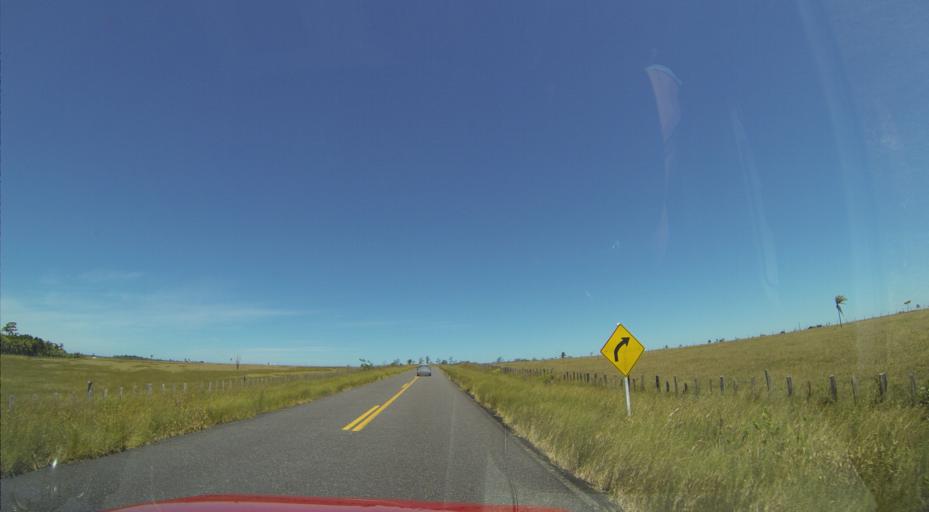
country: BR
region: Bahia
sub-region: Prado
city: Prado
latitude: -17.2447
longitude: -39.3586
